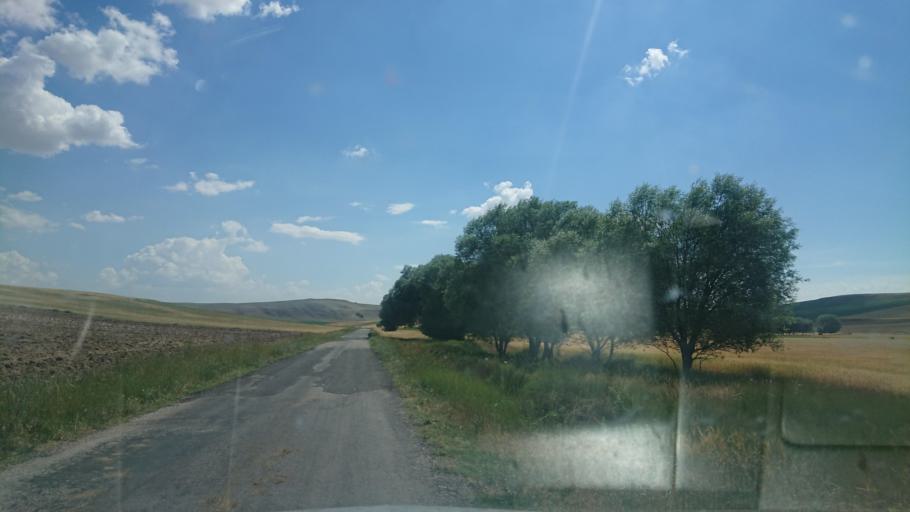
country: TR
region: Aksaray
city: Agacoren
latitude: 38.7938
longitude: 33.8207
